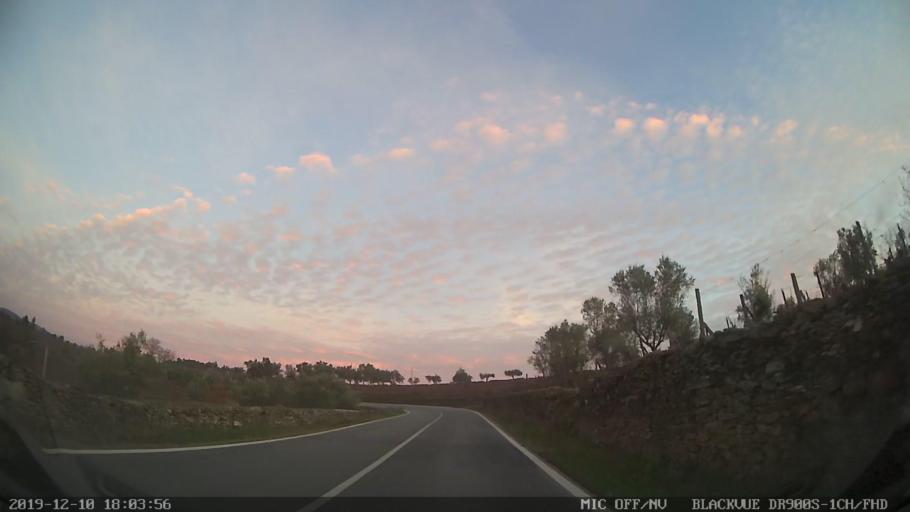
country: PT
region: Vila Real
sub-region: Sabrosa
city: Sabrosa
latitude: 41.2543
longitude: -7.5070
